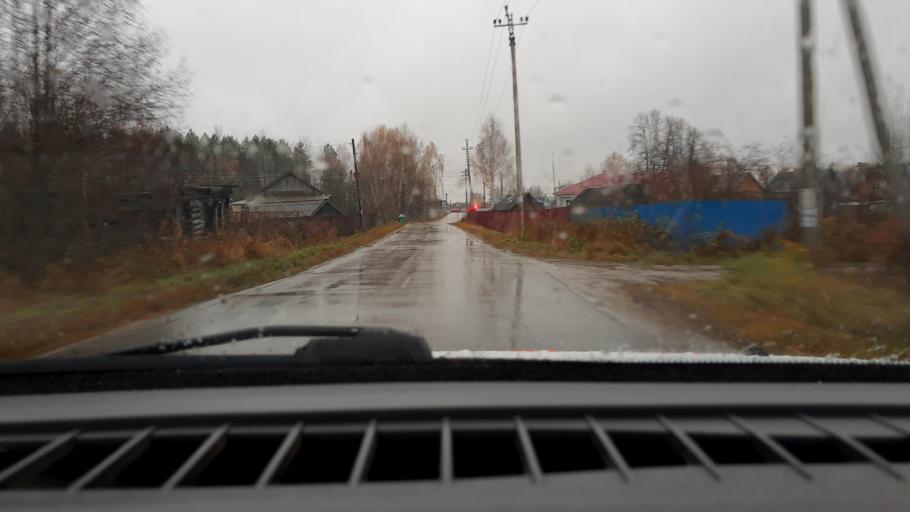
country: RU
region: Nizjnij Novgorod
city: Linda
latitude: 56.6876
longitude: 44.2026
